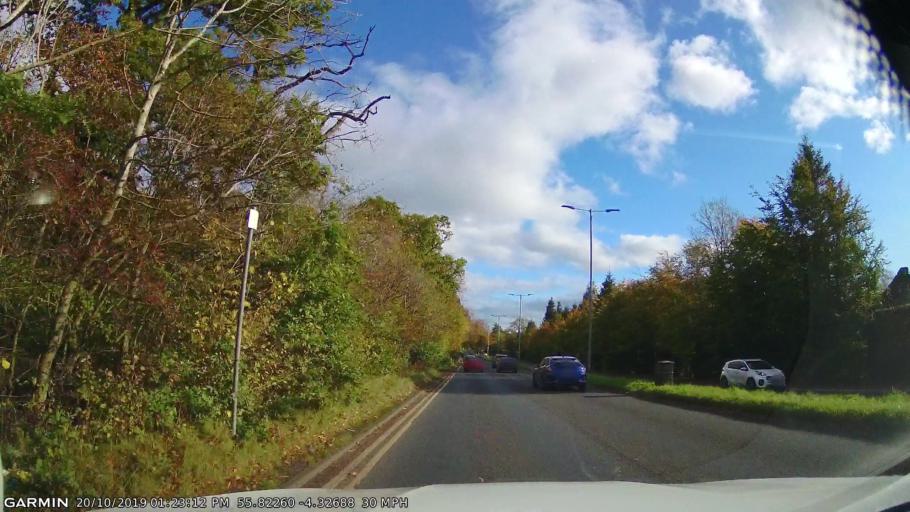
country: GB
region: Scotland
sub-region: East Renfrewshire
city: Giffnock
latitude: 55.8226
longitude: -4.3269
